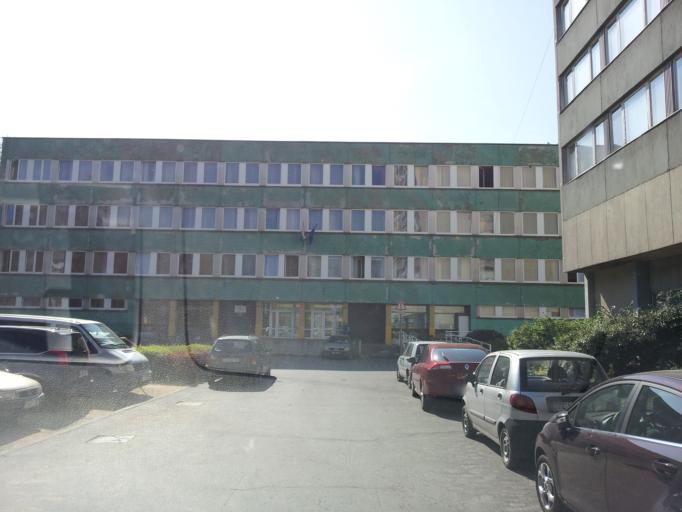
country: HU
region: Fejer
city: Szekesfehervar
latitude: 47.1871
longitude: 18.4182
